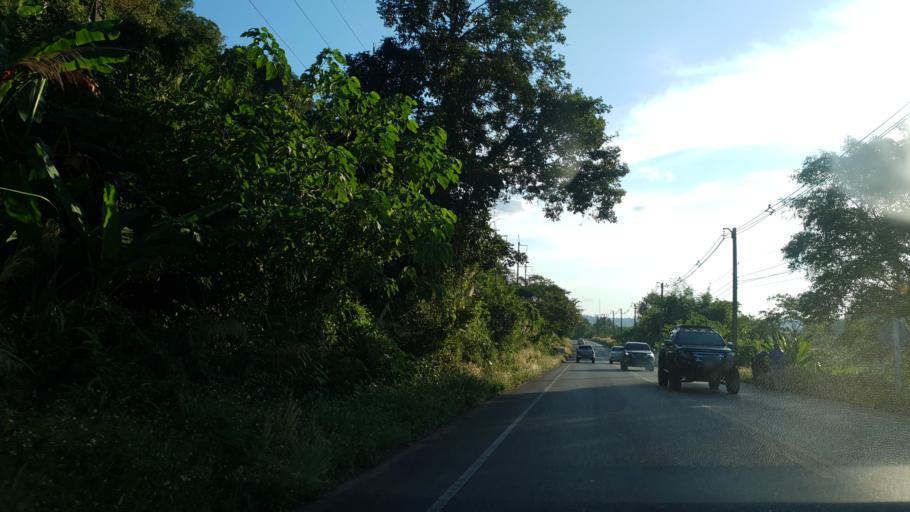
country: TH
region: Loei
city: Dan Sai
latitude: 17.2142
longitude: 101.0201
